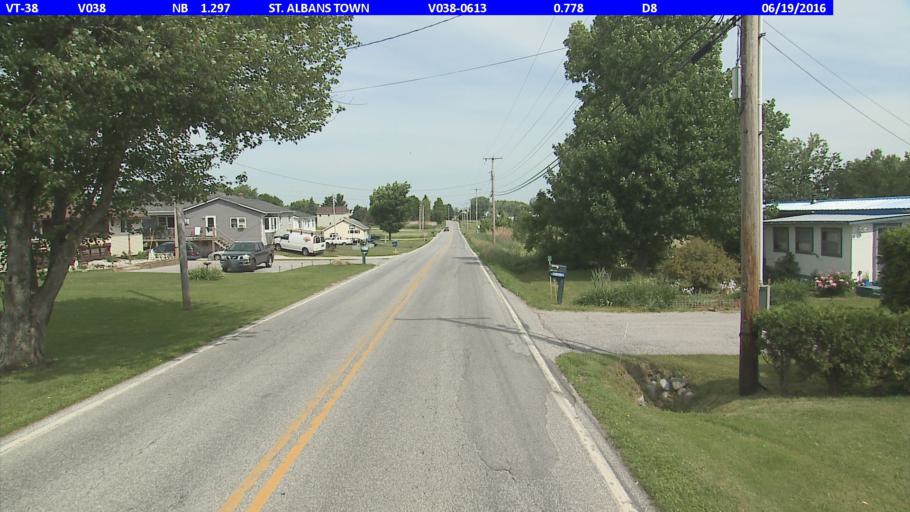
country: US
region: Vermont
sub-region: Franklin County
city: Saint Albans
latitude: 44.8338
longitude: -73.0966
